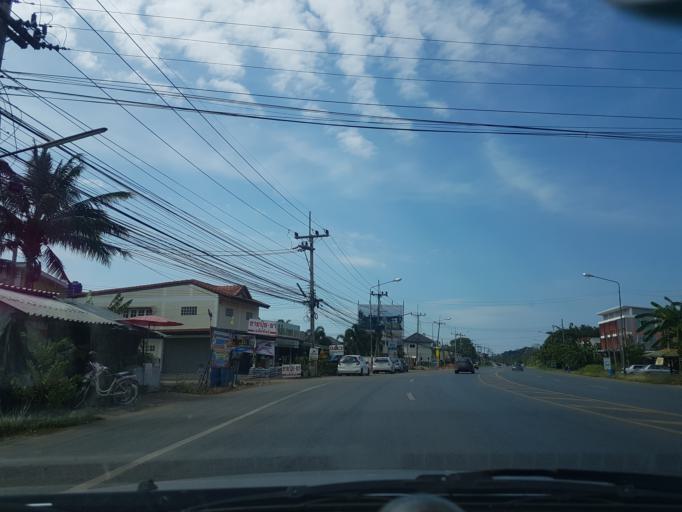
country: TH
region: Lop Buri
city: Lop Buri
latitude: 14.7999
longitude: 100.7260
